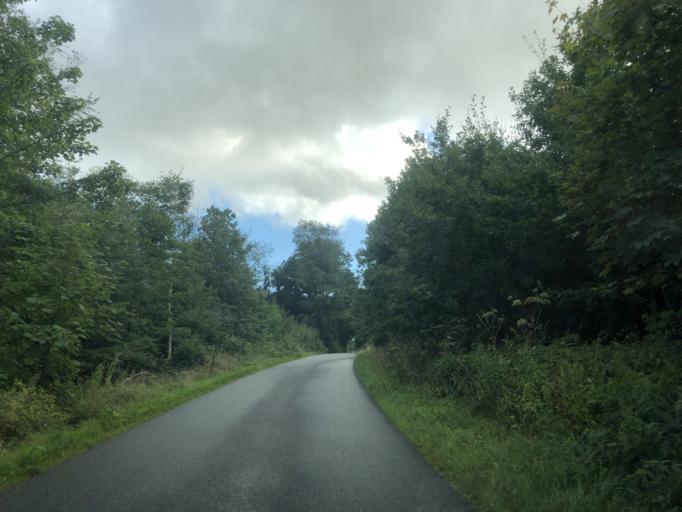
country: DK
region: South Denmark
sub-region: Vejle Kommune
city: Borkop
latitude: 55.6808
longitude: 9.6017
